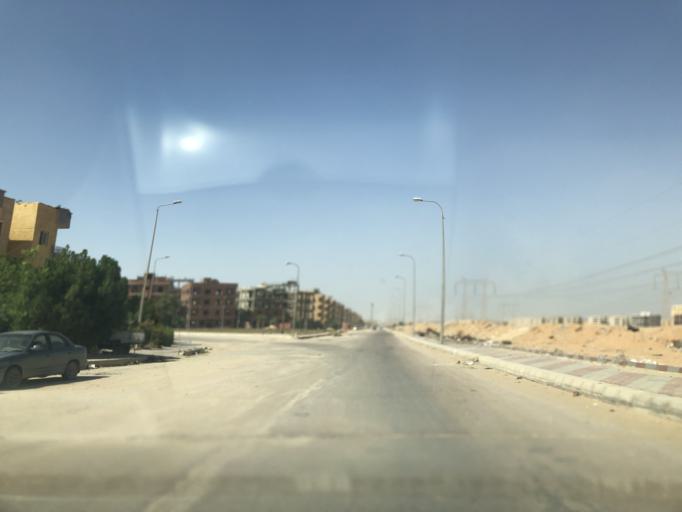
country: EG
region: Al Jizah
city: Madinat Sittah Uktubar
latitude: 29.9156
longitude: 31.0506
